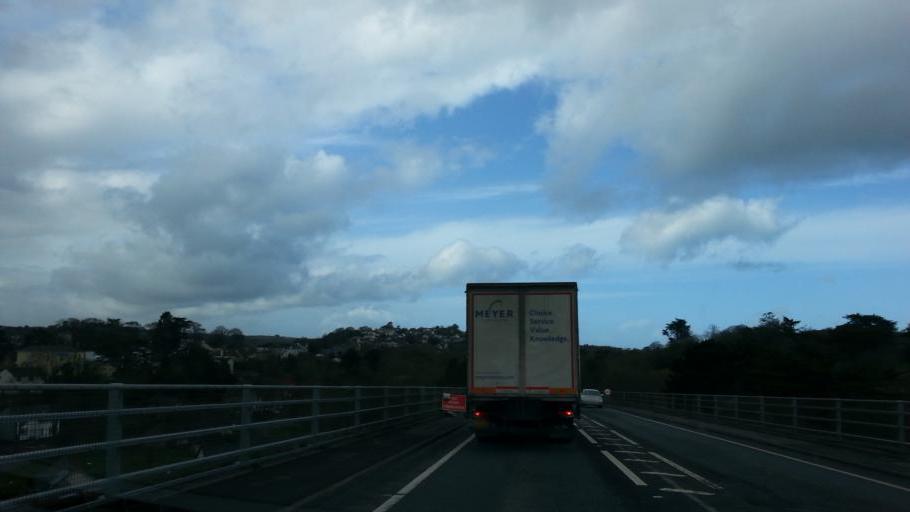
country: GB
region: England
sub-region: Devon
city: Bideford
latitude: 51.0294
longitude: -4.2024
